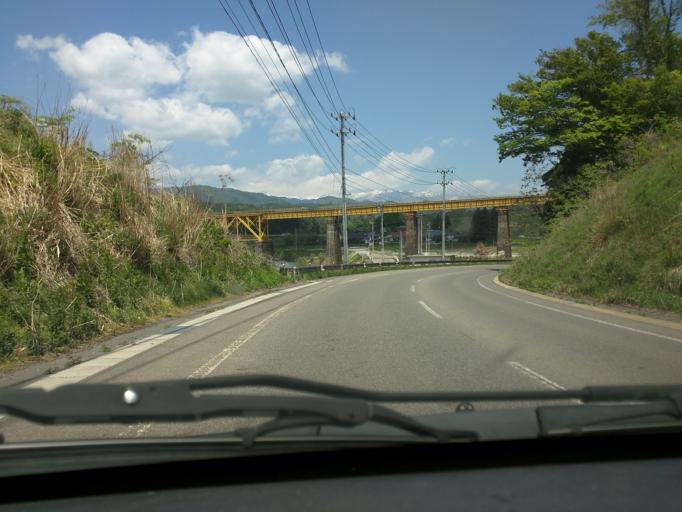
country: JP
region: Fukushima
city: Kitakata
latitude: 37.6393
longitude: 139.7788
